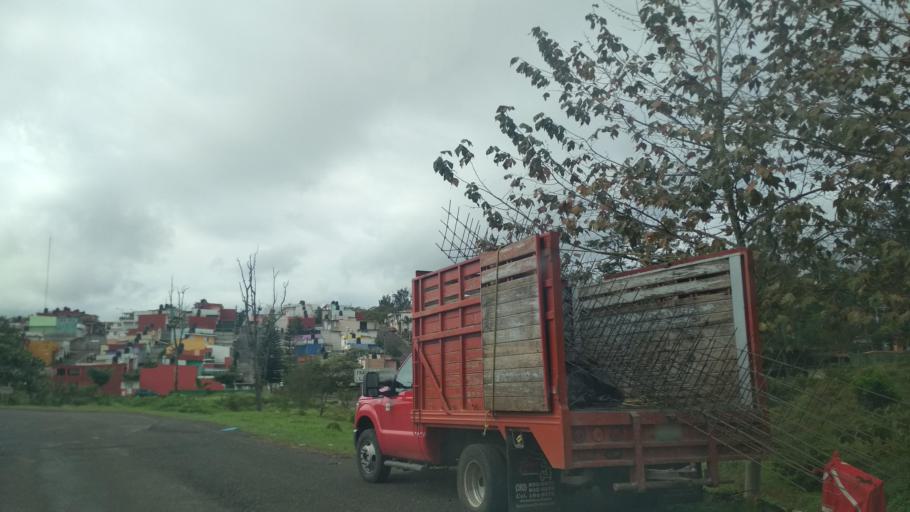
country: MX
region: Veracruz
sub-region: Emiliano Zapata
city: Las Trancas
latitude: 19.5039
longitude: -96.8620
